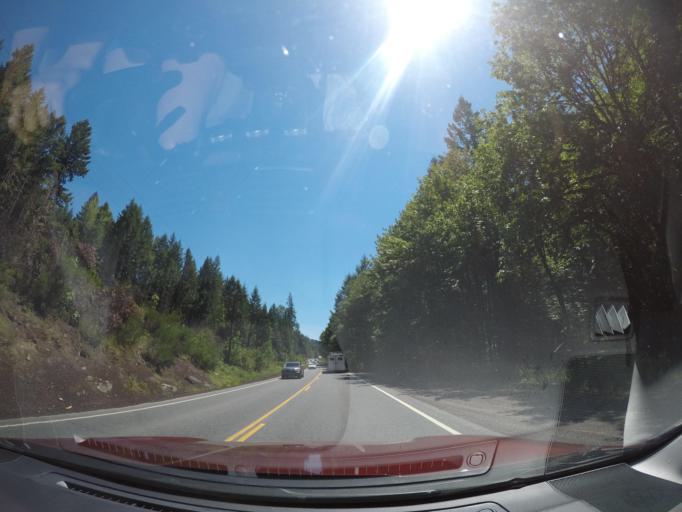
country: US
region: Oregon
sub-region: Linn County
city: Mill City
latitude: 44.7048
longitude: -122.0925
